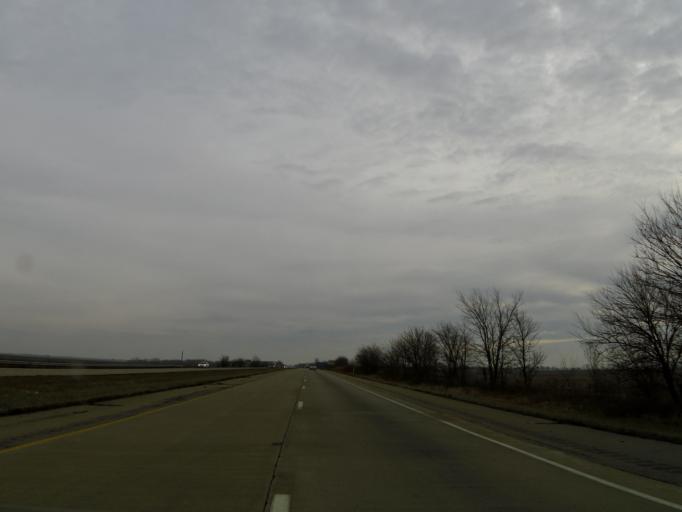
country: US
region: Illinois
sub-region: Vermilion County
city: Danville
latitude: 40.1176
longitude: -87.5257
